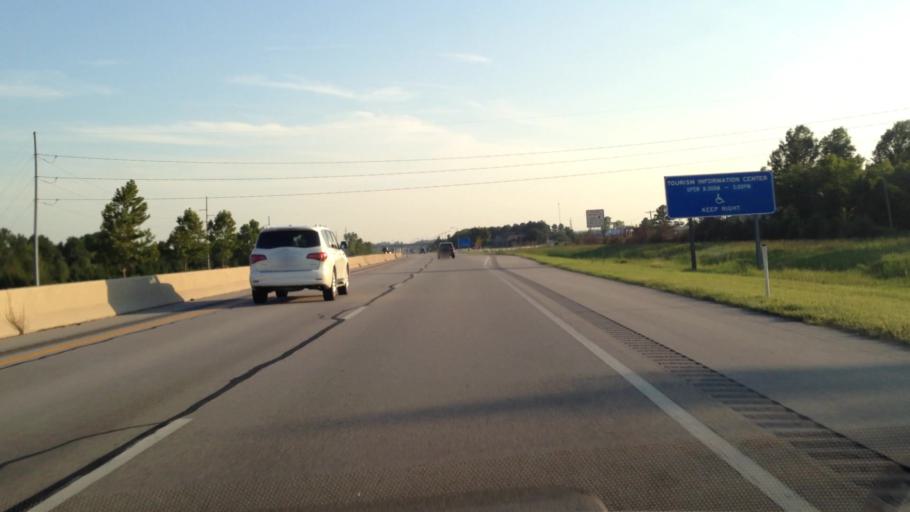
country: US
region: Oklahoma
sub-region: Ottawa County
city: Miami
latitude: 36.8796
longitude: -94.8434
